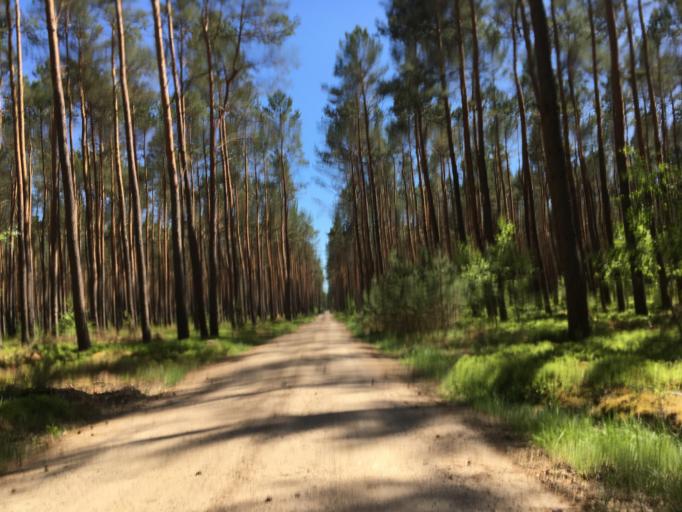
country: DE
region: Brandenburg
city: Friedrichswalde
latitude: 52.9779
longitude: 13.6300
